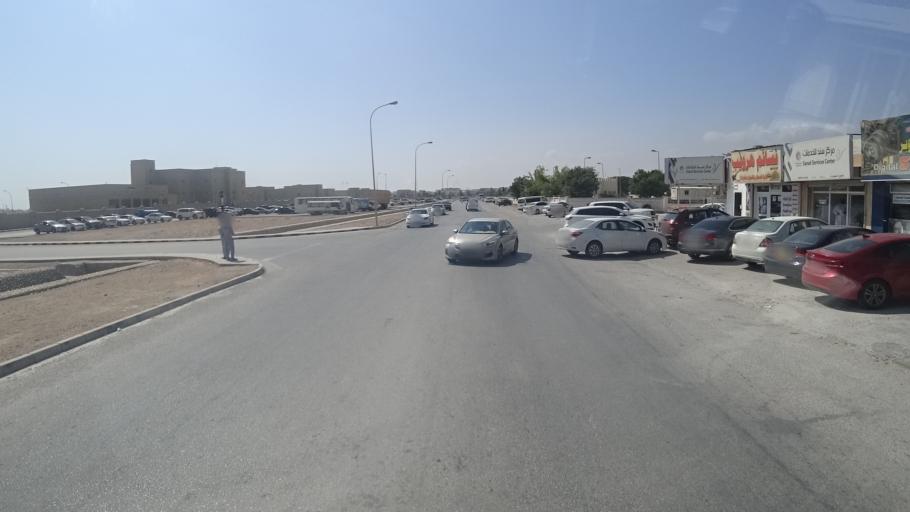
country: OM
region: Zufar
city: Salalah
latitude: 17.0184
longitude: 54.0406
